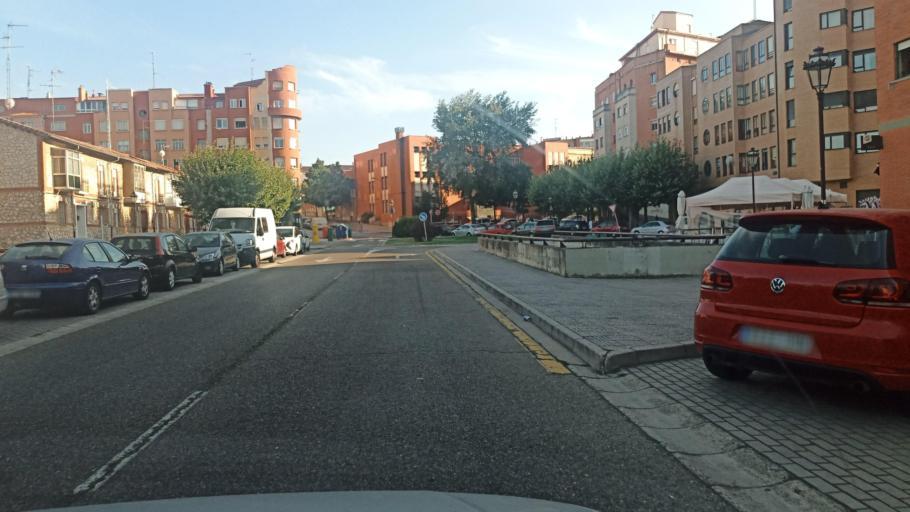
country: ES
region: Castille and Leon
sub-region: Provincia de Burgos
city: Burgos
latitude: 42.3358
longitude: -3.6974
